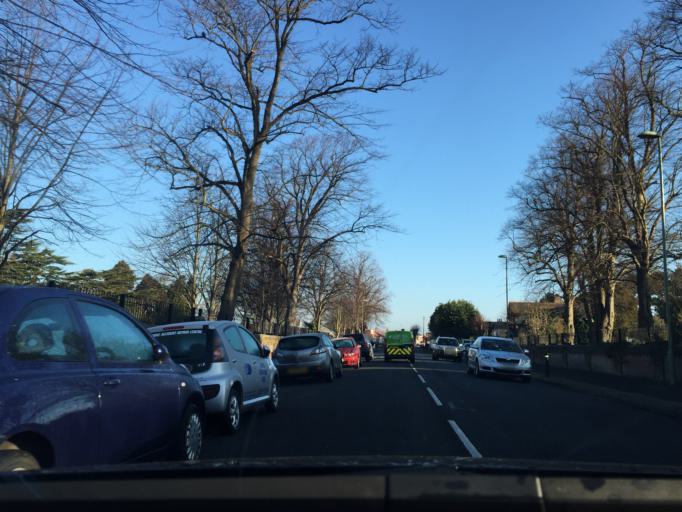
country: GB
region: England
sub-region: Hampshire
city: Gosport
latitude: 50.7973
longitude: -1.1487
